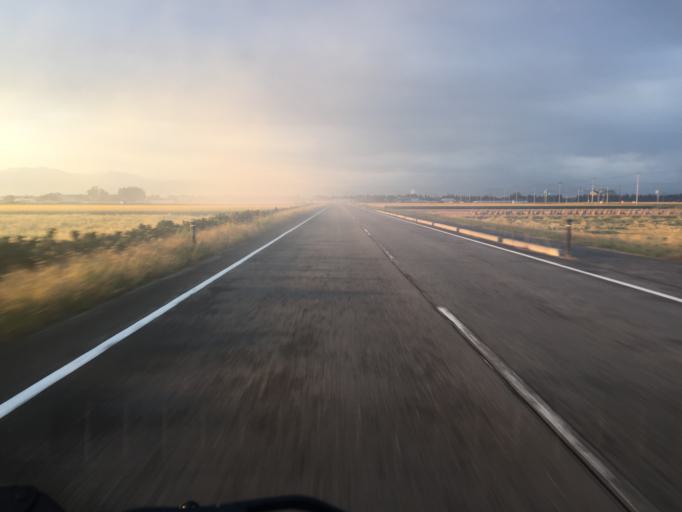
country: JP
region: Fukushima
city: Kitakata
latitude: 37.5431
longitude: 139.8988
